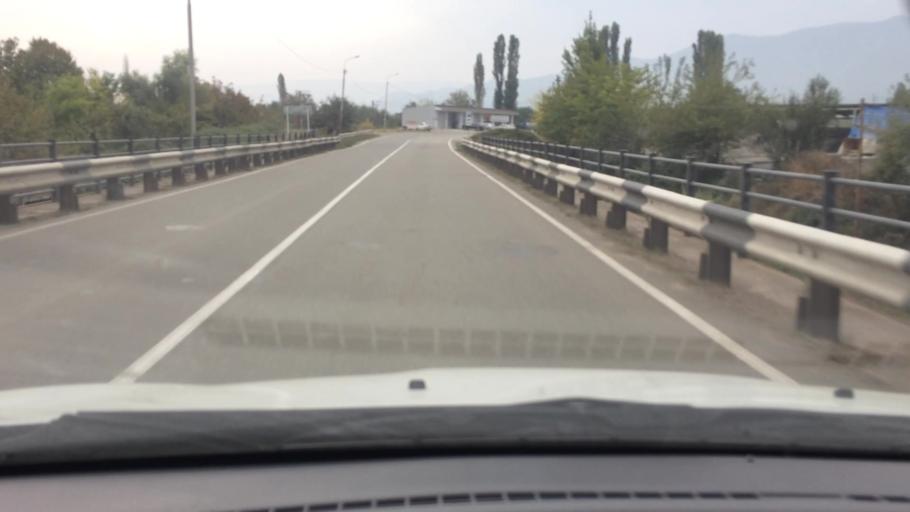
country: AM
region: Tavush
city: Bagratashen
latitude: 41.2554
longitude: 44.7988
